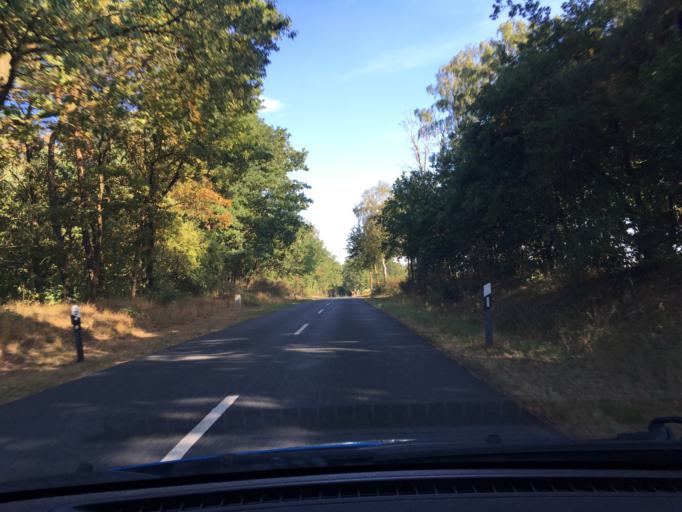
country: DE
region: Lower Saxony
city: Dahlenburg
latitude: 53.2028
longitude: 10.7128
